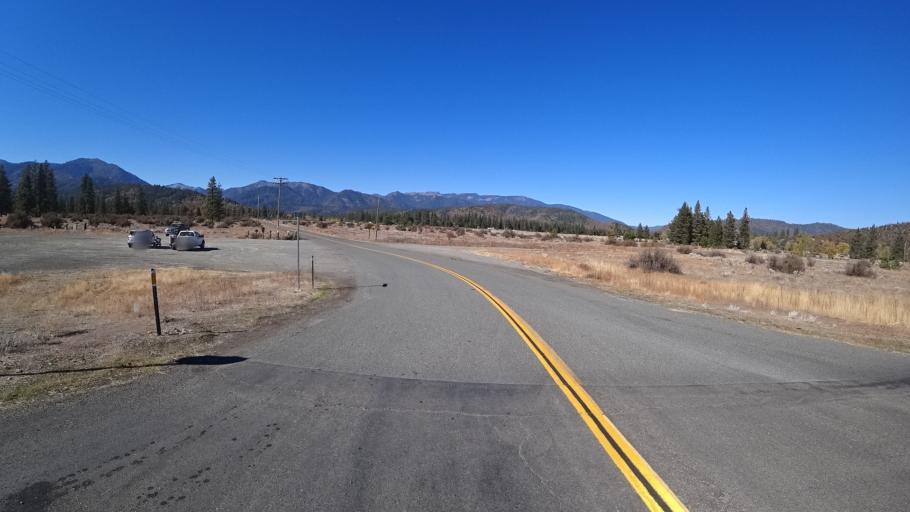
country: US
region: California
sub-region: Siskiyou County
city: Yreka
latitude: 41.5408
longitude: -122.9060
